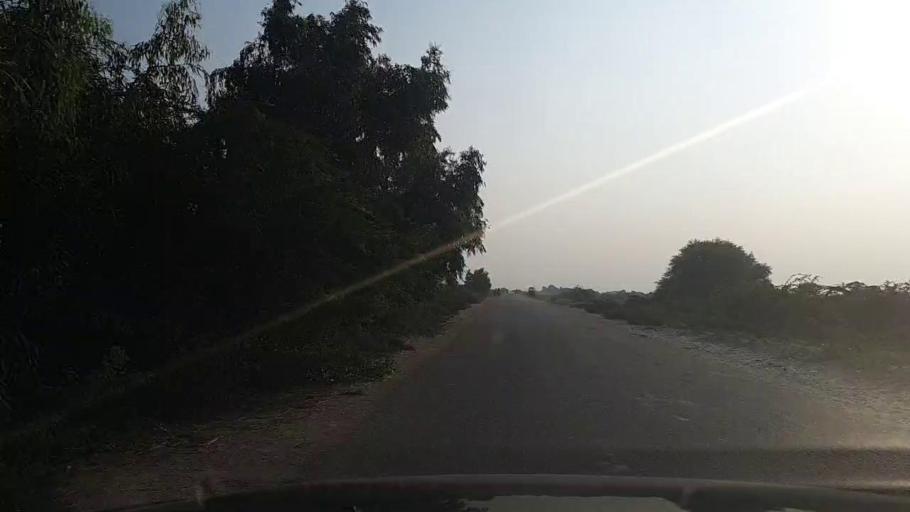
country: PK
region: Sindh
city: Mirpur Sakro
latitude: 24.4975
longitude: 67.8126
